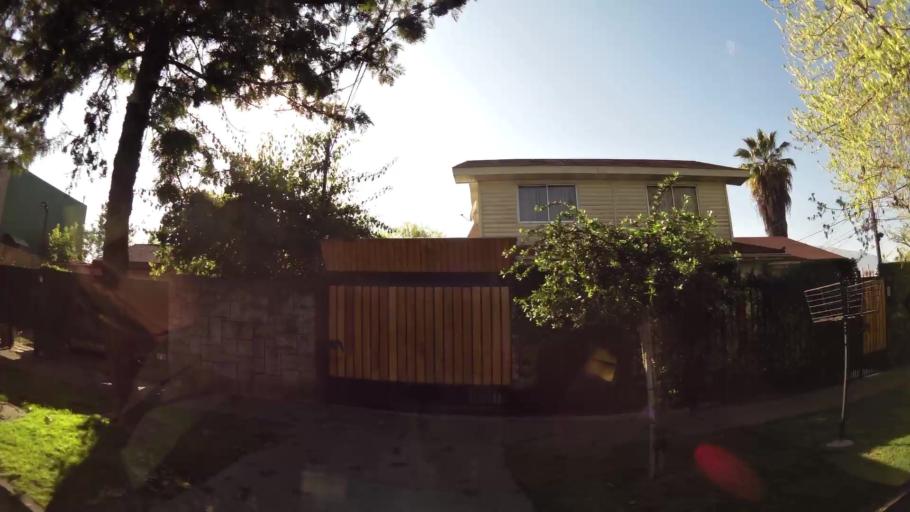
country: CL
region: Santiago Metropolitan
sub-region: Provincia de Santiago
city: Villa Presidente Frei, Nunoa, Santiago, Chile
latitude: -33.4573
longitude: -70.5616
